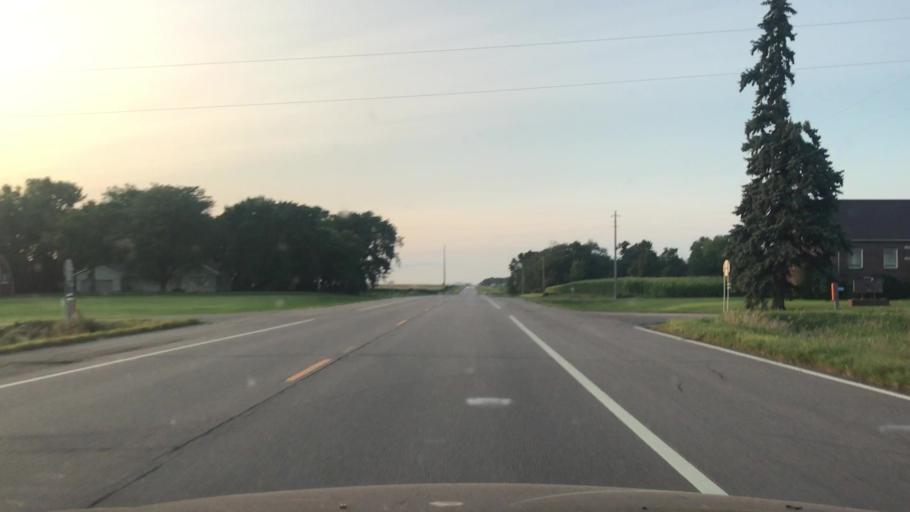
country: US
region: Minnesota
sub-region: Redwood County
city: Redwood Falls
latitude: 44.4268
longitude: -95.1175
